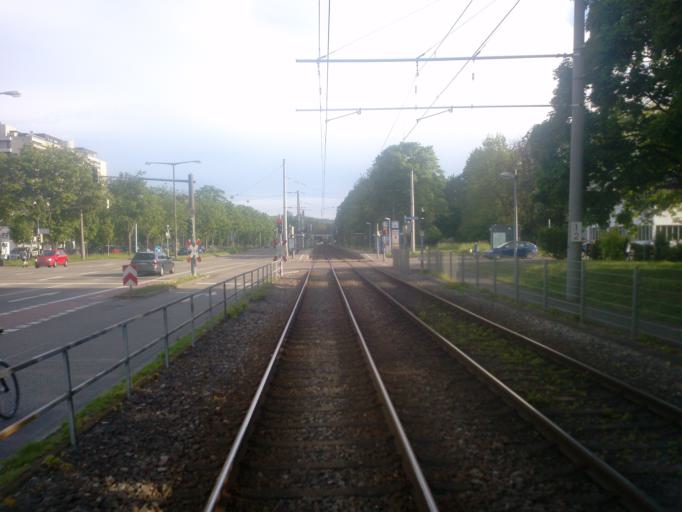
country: DE
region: Baden-Wuerttemberg
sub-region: Karlsruhe Region
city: Karlsruhe
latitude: 48.9851
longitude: 8.4035
